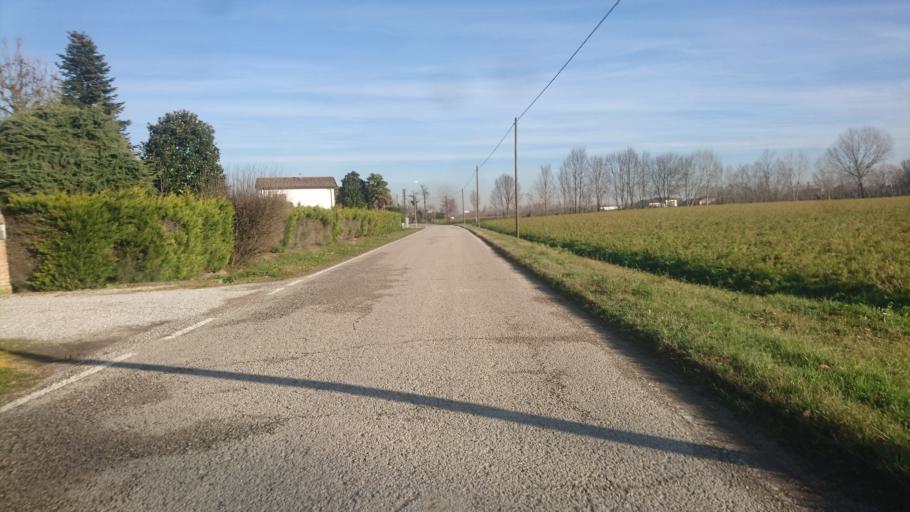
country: IT
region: Veneto
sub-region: Provincia di Padova
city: Tremignon
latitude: 45.5124
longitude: 11.7906
